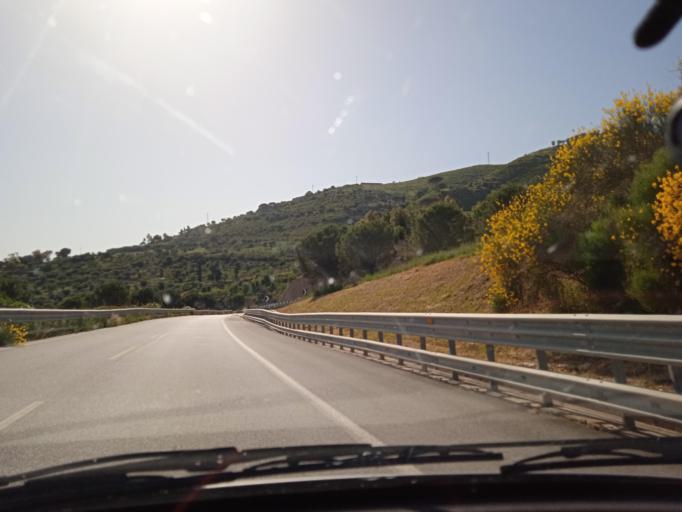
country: IT
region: Sicily
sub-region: Messina
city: Santo Stefano di Camastra
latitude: 38.0063
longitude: 14.3254
